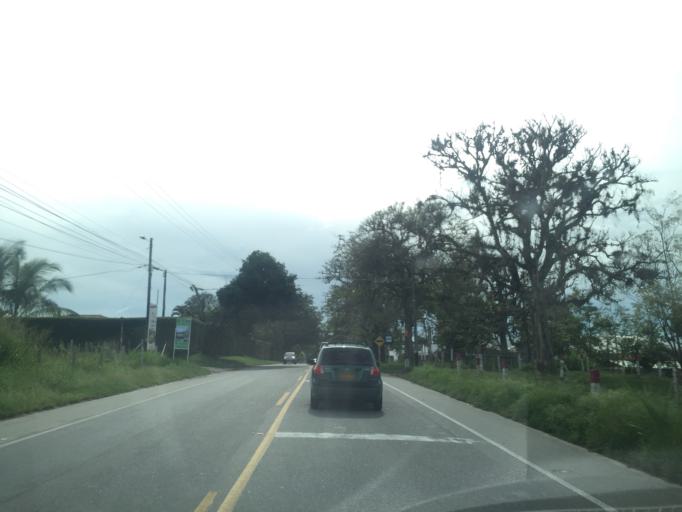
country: CO
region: Quindio
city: La Tebaida
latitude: 4.4776
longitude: -75.7543
